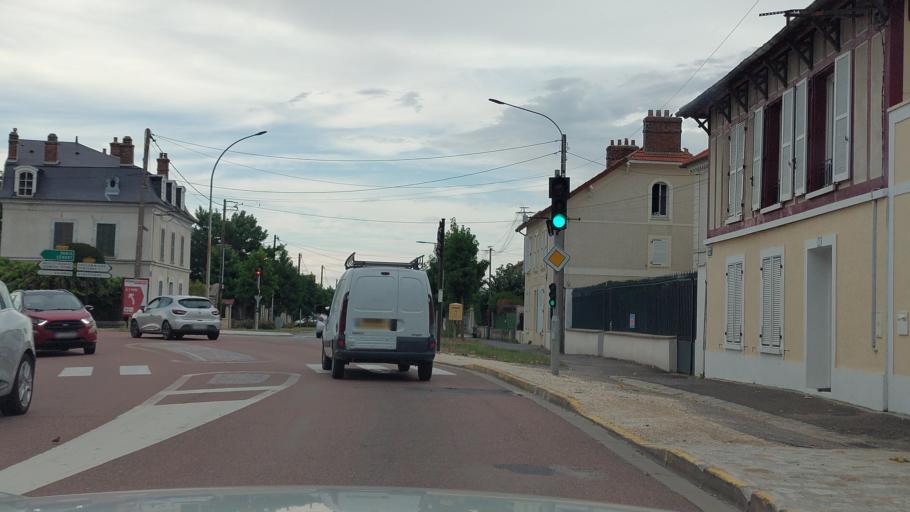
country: FR
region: Ile-de-France
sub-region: Departement de Seine-et-Marne
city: Mormant
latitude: 48.6103
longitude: 2.8906
